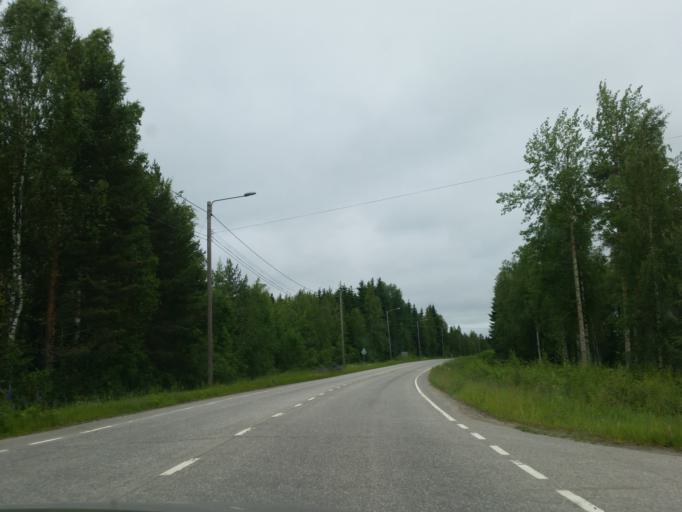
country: FI
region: Northern Savo
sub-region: Koillis-Savo
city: Kaavi
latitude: 62.9747
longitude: 28.4956
